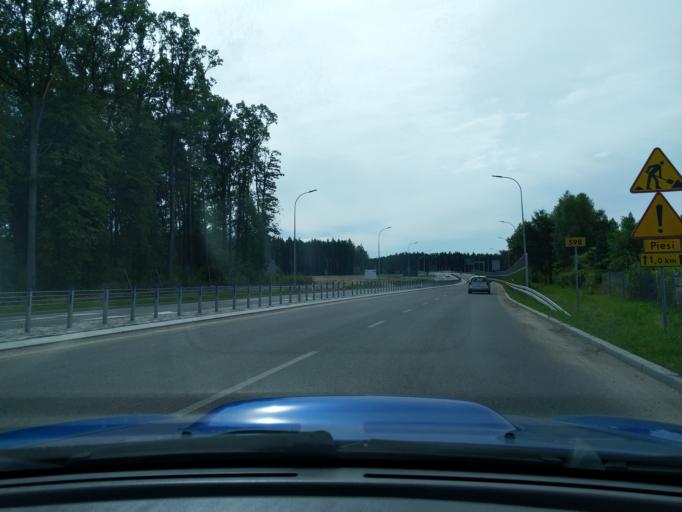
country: PL
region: Warmian-Masurian Voivodeship
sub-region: Powiat olsztynski
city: Olsztyn
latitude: 53.7141
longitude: 20.5097
